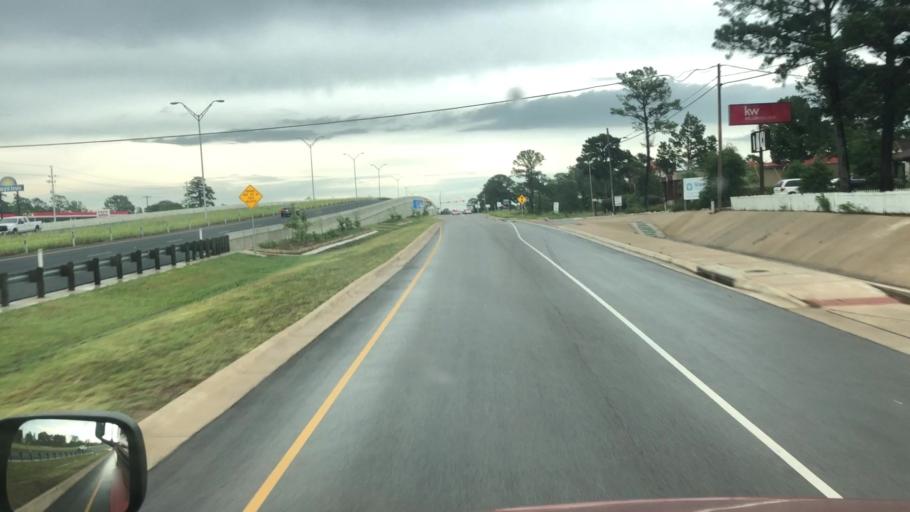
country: US
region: Texas
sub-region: Bastrop County
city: Bastrop
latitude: 30.1032
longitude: -97.2881
